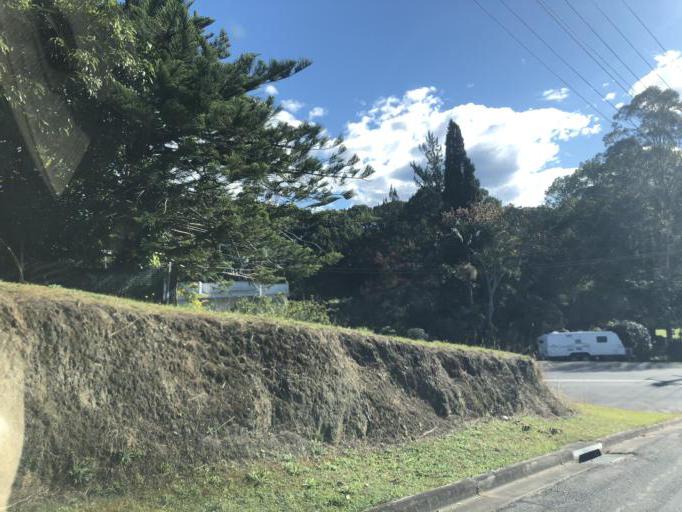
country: AU
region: New South Wales
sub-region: Nambucca Shire
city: Bowraville
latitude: -30.6418
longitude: 152.8551
